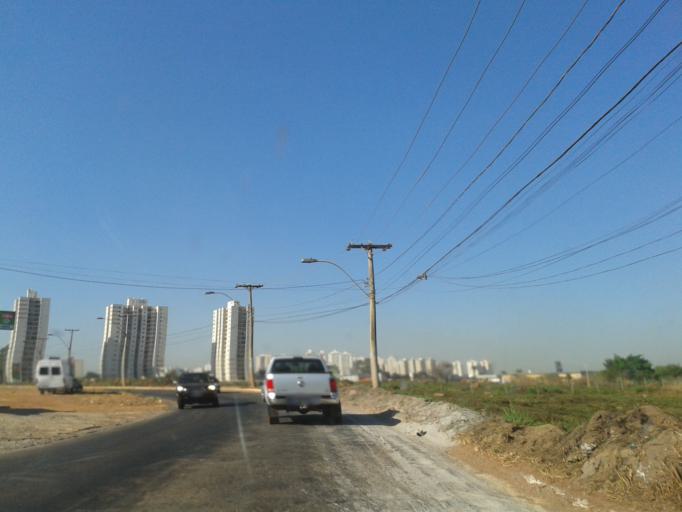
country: BR
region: Goias
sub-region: Goiania
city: Goiania
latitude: -16.6904
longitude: -49.3283
